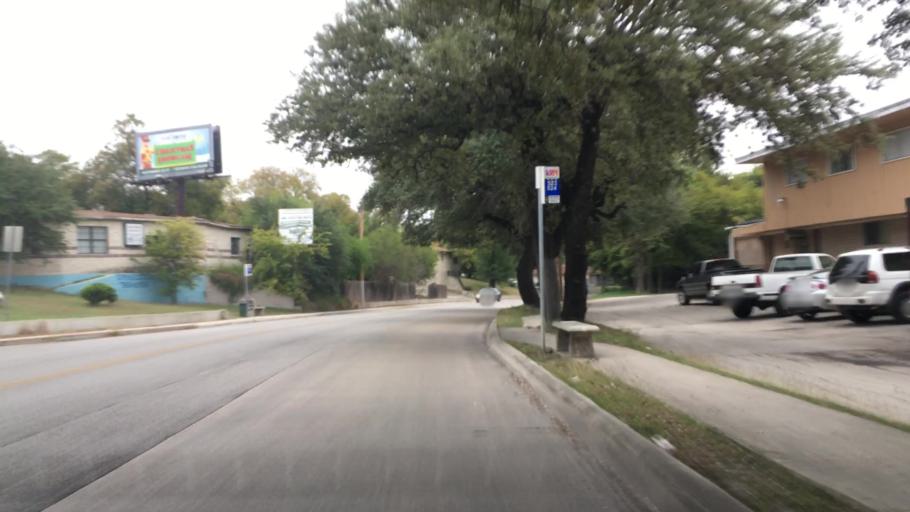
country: US
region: Texas
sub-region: Bexar County
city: Balcones Heights
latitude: 29.4832
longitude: -98.5560
